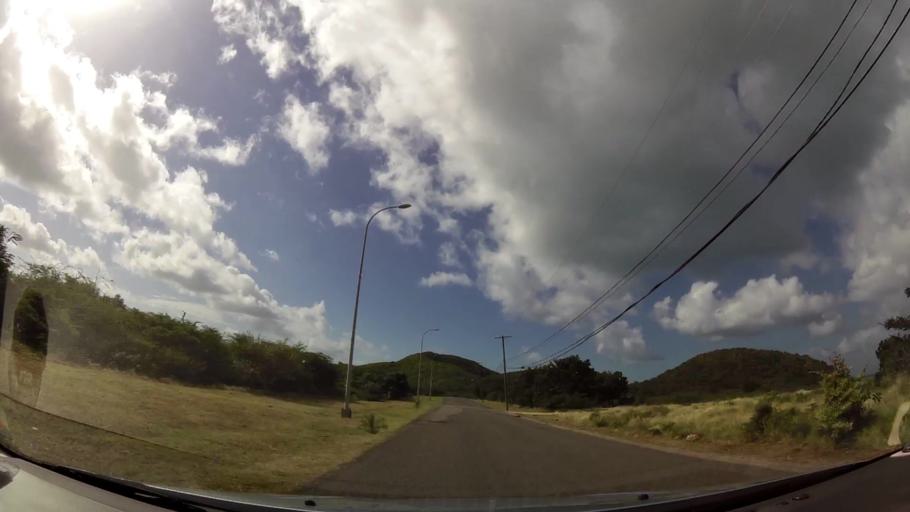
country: AG
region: Saint John
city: Saint John's
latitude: 17.1179
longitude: -61.8661
